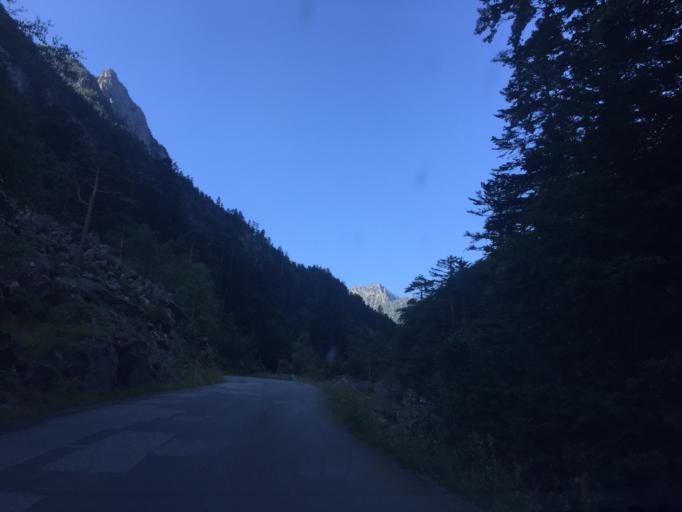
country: FR
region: Midi-Pyrenees
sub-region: Departement des Hautes-Pyrenees
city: Cauterets
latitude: 42.8664
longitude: -0.1154
